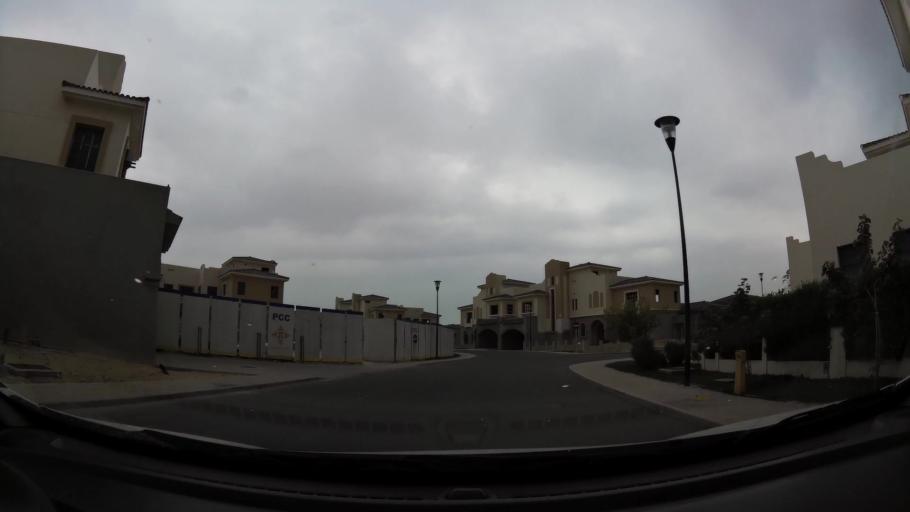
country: BH
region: Northern
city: Ar Rifa'
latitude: 26.0841
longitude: 50.5580
